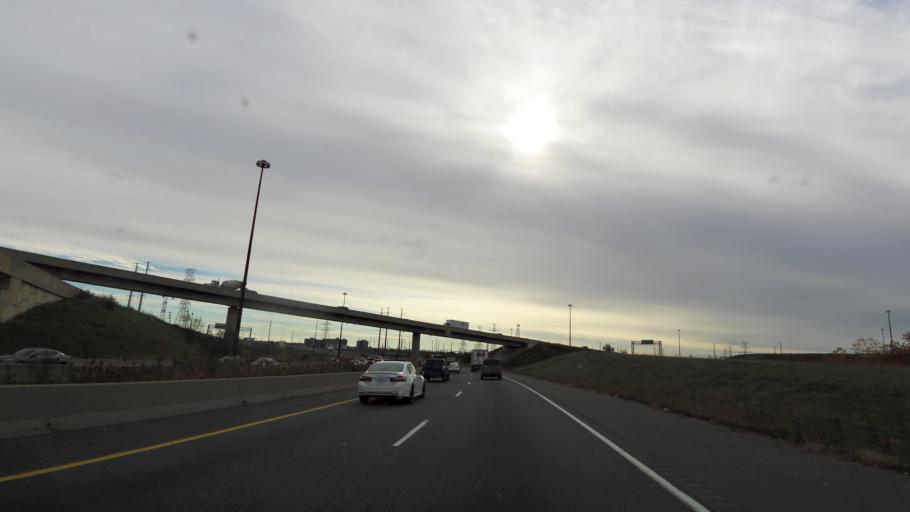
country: CA
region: Ontario
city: Burlington
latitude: 43.3376
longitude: -79.8288
